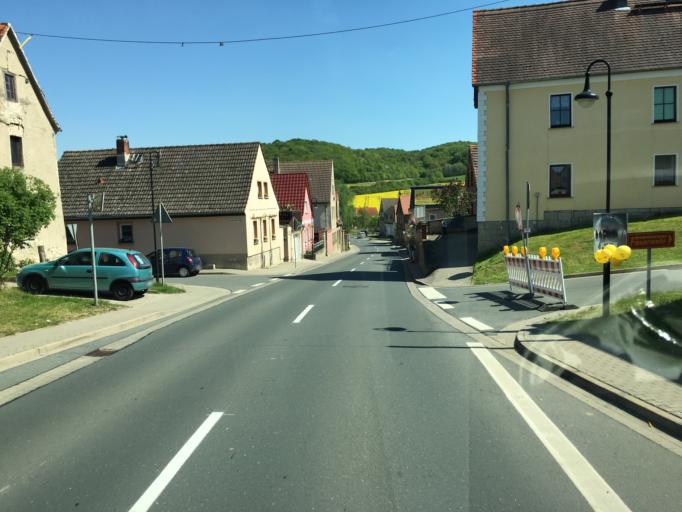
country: DE
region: Saxony-Anhalt
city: Balgstadt
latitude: 51.2051
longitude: 11.7327
